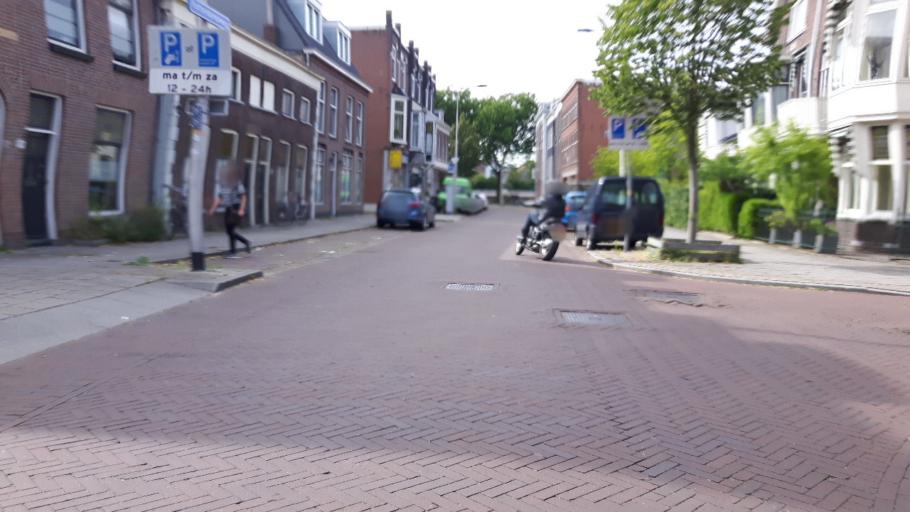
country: NL
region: South Holland
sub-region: Gemeente Delft
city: Delft
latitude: 52.0052
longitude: 4.3636
